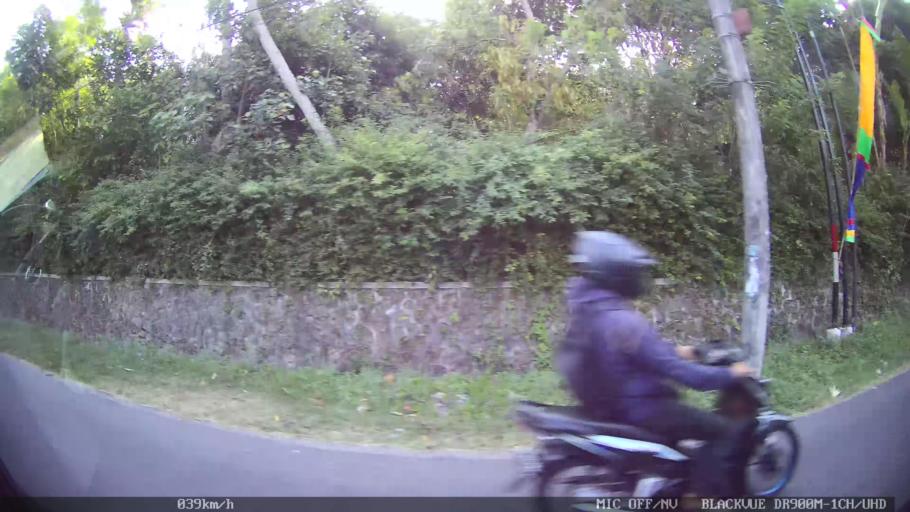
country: ID
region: Daerah Istimewa Yogyakarta
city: Bantul
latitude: -7.8766
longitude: 110.3149
